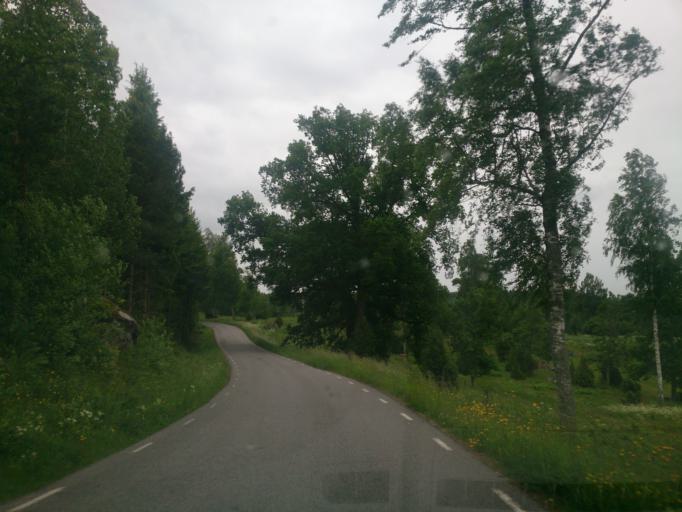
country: SE
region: OEstergoetland
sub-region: Atvidabergs Kommun
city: Atvidaberg
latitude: 58.2824
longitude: 16.0971
